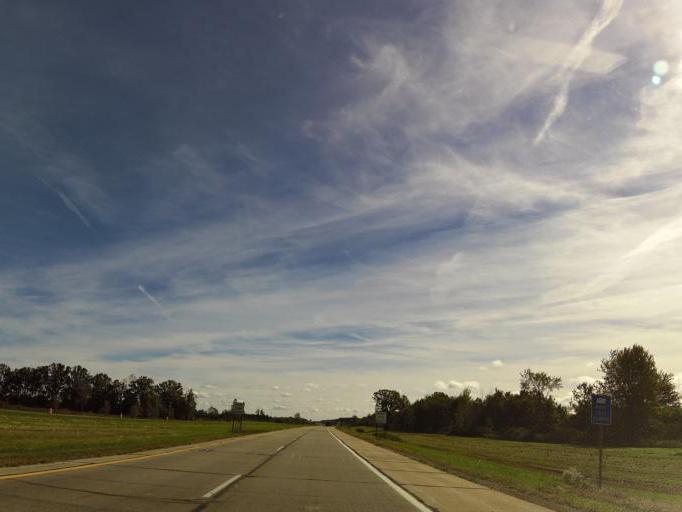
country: US
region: Michigan
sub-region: Macomb County
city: Memphis
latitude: 42.9780
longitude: -82.8020
